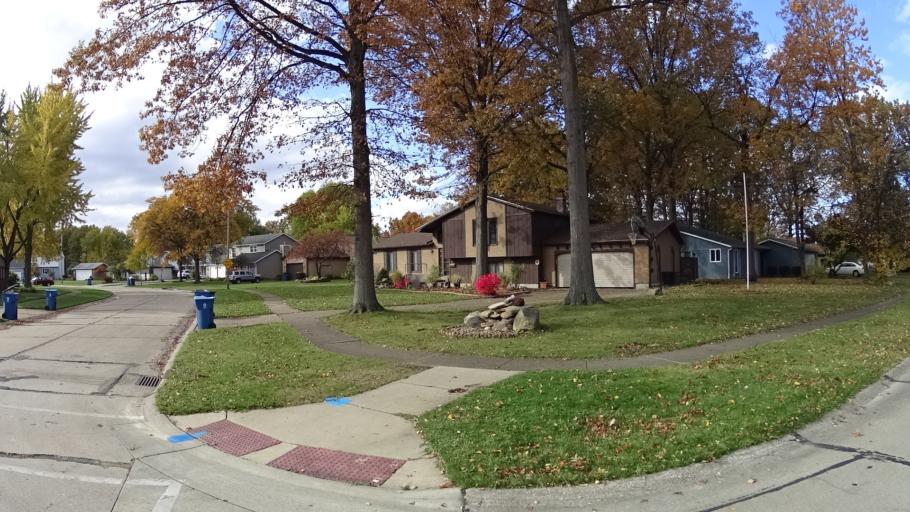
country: US
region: Ohio
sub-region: Lorain County
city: Lorain
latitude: 41.4239
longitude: -82.2002
